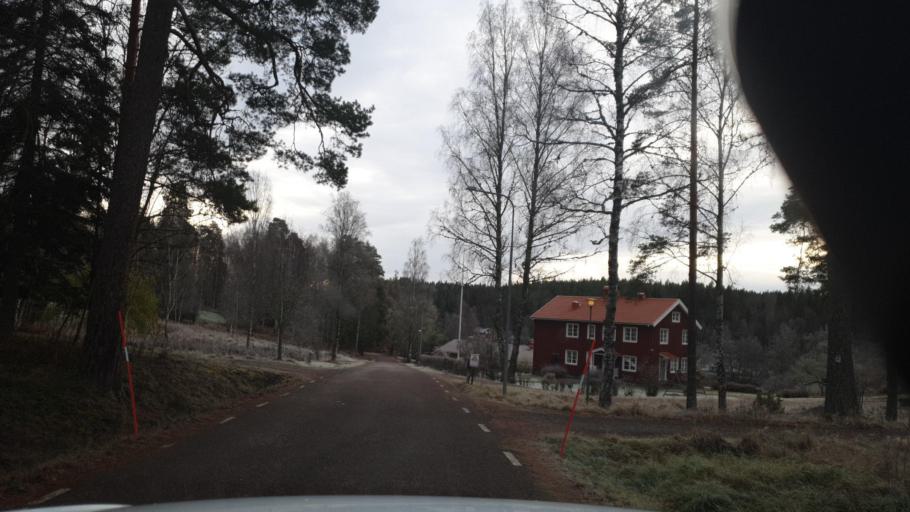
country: SE
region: Vaermland
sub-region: Sunne Kommun
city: Sunne
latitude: 59.6209
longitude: 12.9598
